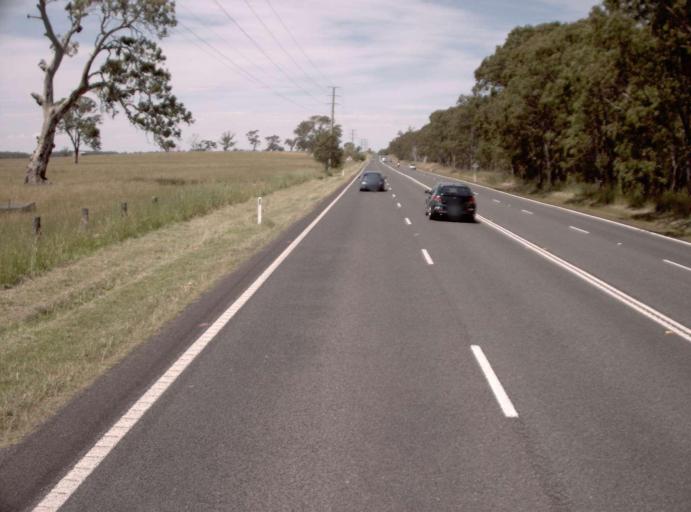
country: AU
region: Victoria
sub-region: Latrobe
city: Traralgon
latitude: -38.1778
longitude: 146.6359
